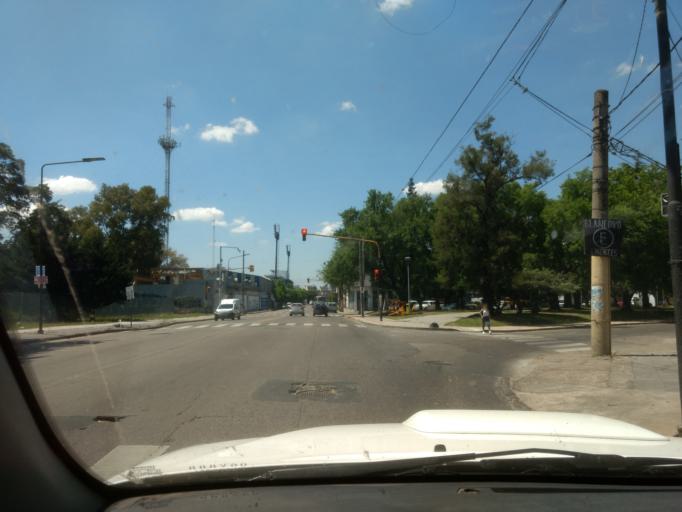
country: AR
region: Buenos Aires
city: Caseros
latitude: -34.6155
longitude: -58.5368
